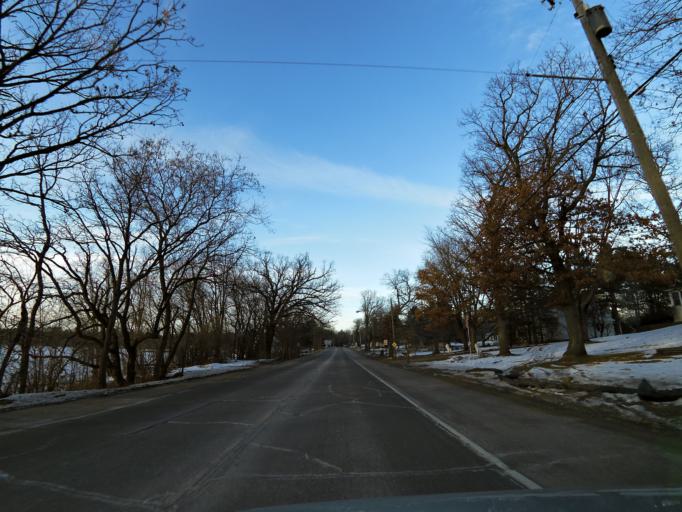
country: US
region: Minnesota
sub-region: Washington County
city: Lake Elmo
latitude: 44.9895
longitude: -92.8804
